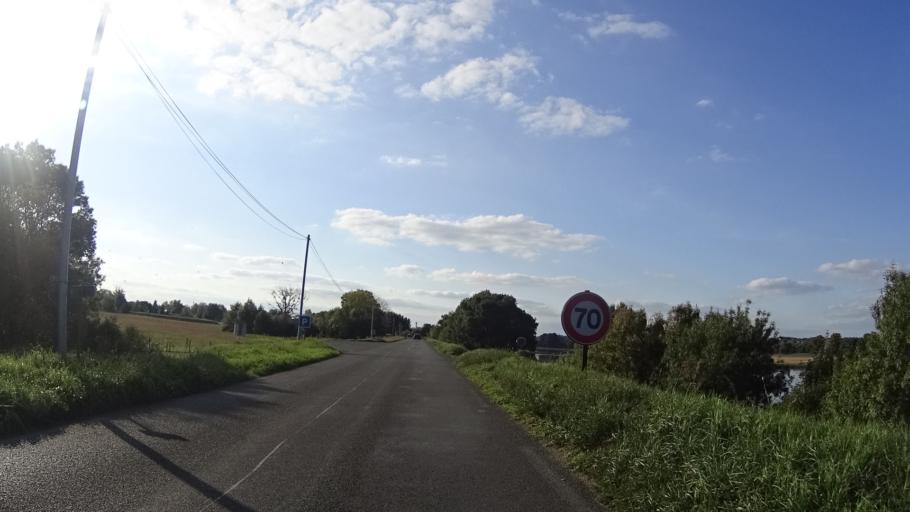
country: FR
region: Pays de la Loire
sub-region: Departement de Maine-et-Loire
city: Ingrandes
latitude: 47.3989
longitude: -0.9006
